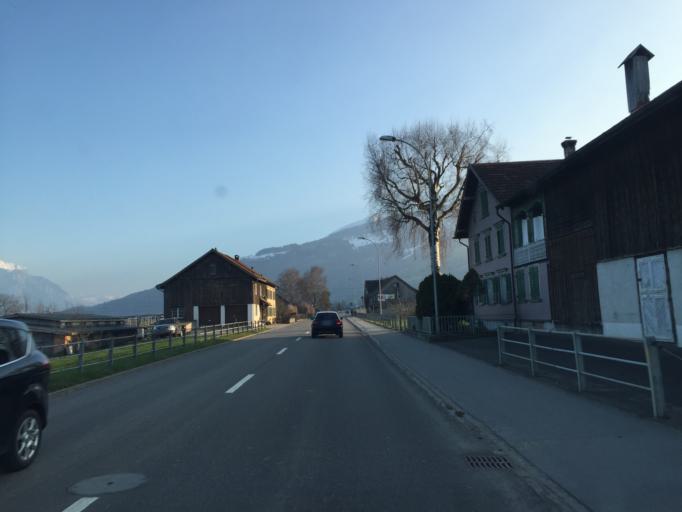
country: CH
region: Saint Gallen
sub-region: Wahlkreis Werdenberg
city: Gams
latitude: 47.1975
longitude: 9.4442
